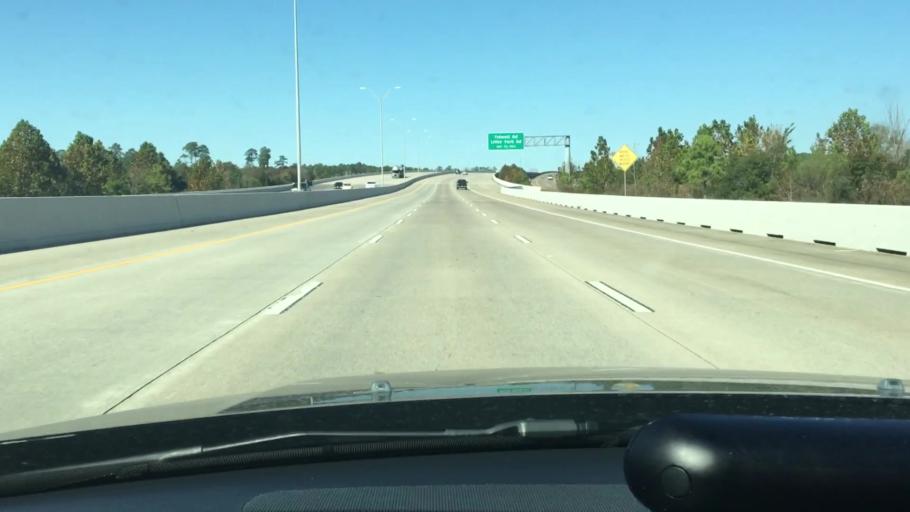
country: US
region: Texas
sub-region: Harris County
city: Sheldon
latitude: 29.8392
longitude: -95.1820
